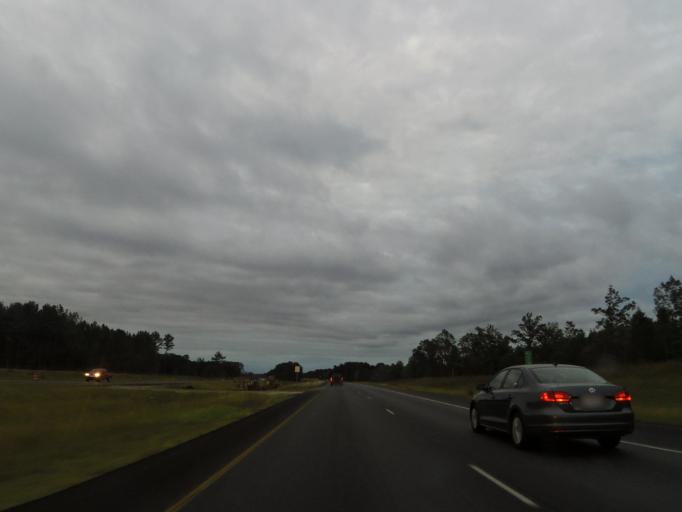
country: US
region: Alabama
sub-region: Saint Clair County
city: Steele
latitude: 33.9478
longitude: -86.1567
